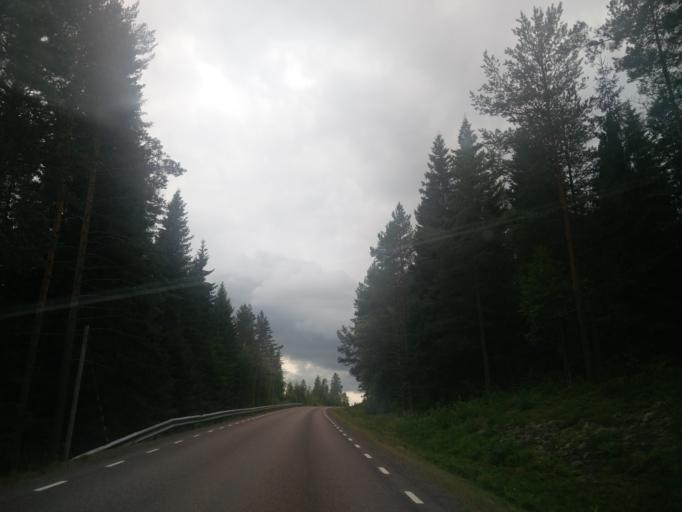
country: SE
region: Vaermland
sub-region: Arvika Kommun
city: Arvika
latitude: 59.9502
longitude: 12.6979
